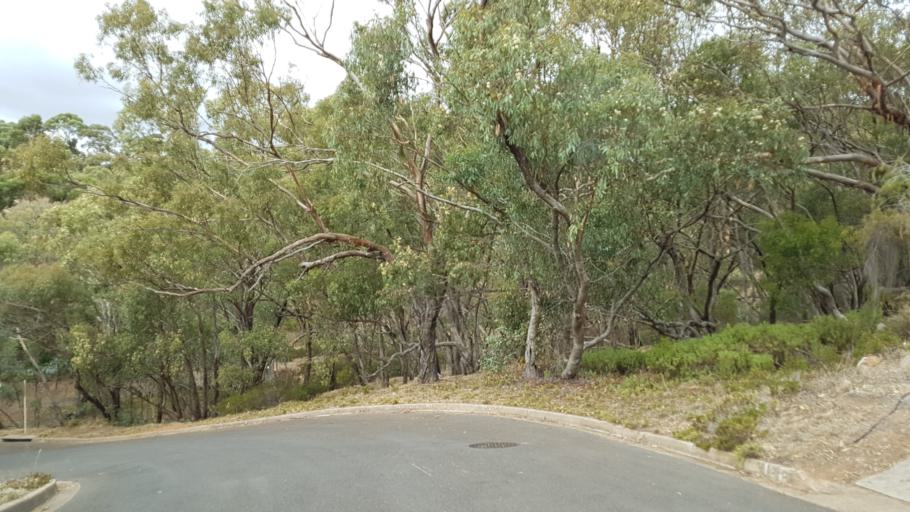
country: AU
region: South Australia
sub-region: Mitcham
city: Clapham
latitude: -35.0068
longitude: 138.5955
